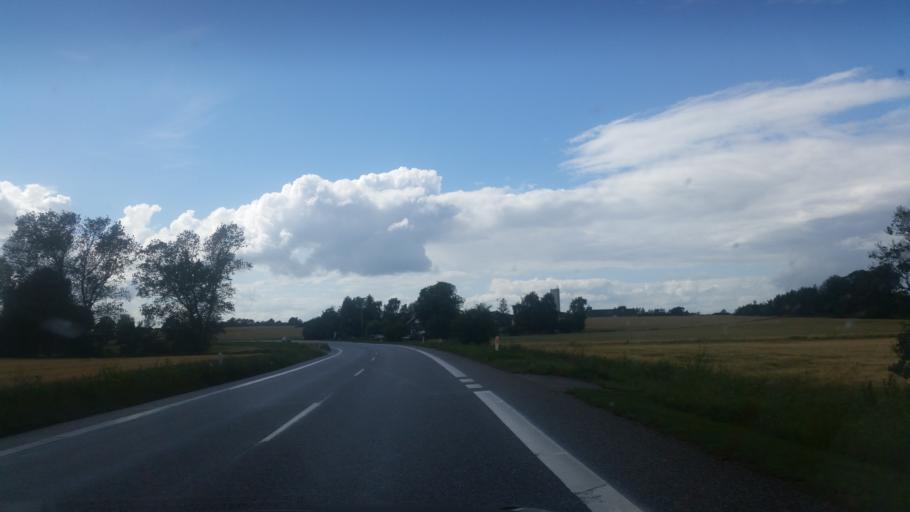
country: DK
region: Zealand
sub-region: Holbaek Kommune
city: Svinninge
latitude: 55.7271
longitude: 11.5794
